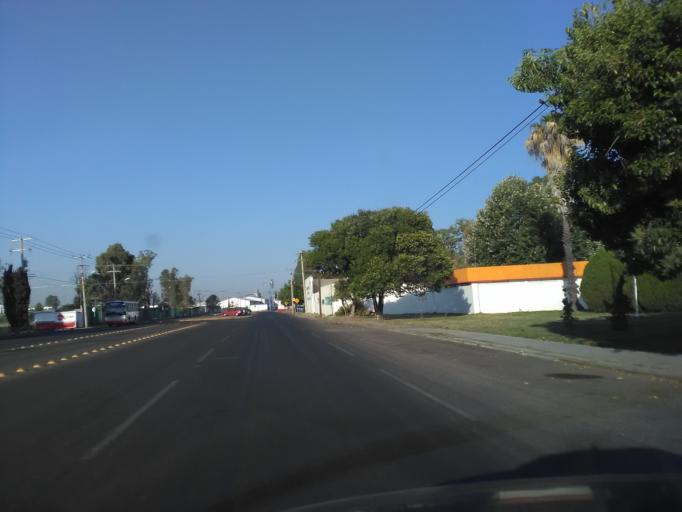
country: MX
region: Durango
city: Victoria de Durango
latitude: 24.0652
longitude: -104.6090
